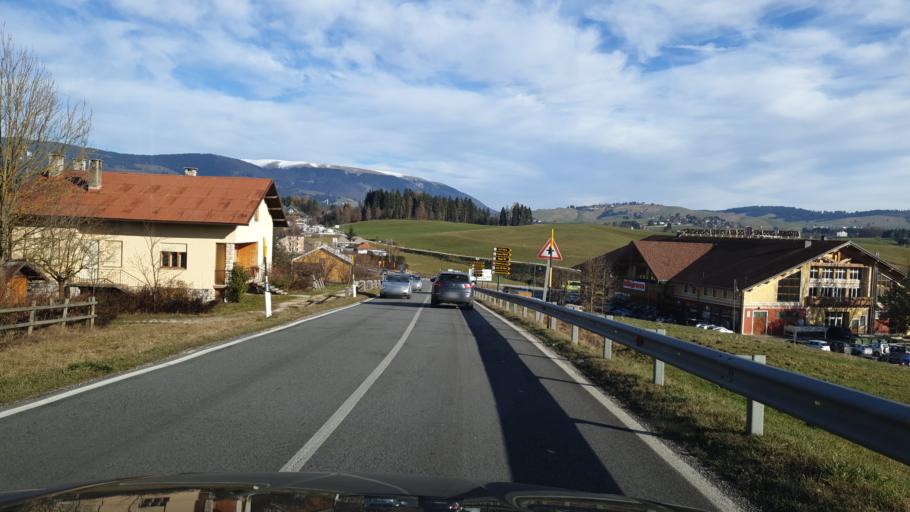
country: IT
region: Veneto
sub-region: Provincia di Vicenza
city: Asiago
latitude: 45.8682
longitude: 11.4945
